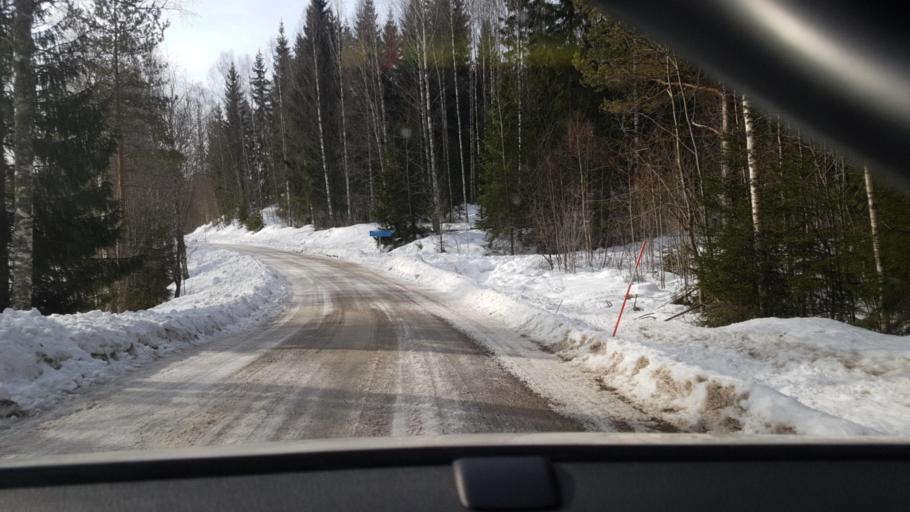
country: NO
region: Hedmark
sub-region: Eidskog
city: Skotterud
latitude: 59.8746
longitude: 11.9771
